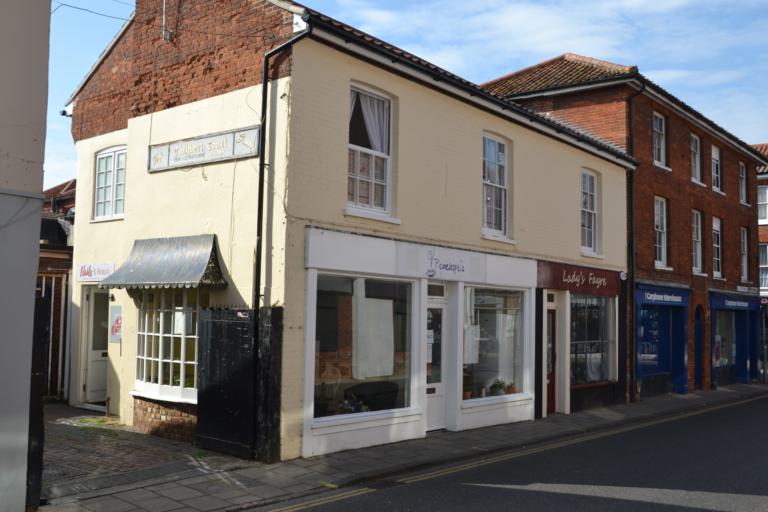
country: GB
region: England
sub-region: Norfolk
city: East Dereham
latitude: 52.6804
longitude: 0.9417
